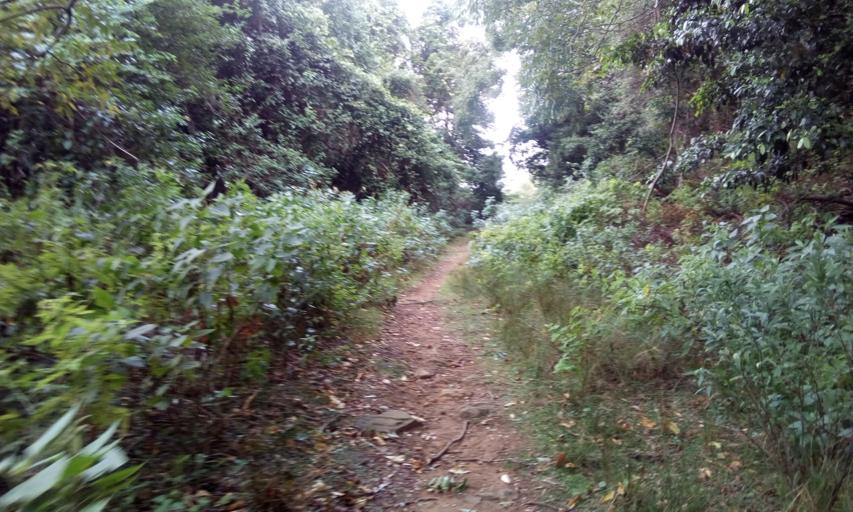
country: AU
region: New South Wales
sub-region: Wollongong
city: Keiraville
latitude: -34.4041
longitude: 150.8615
